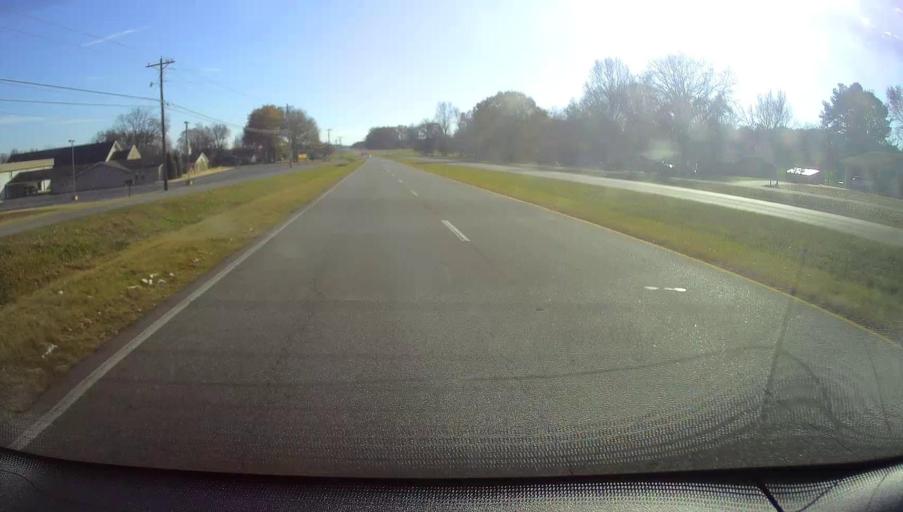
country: US
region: Alabama
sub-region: Limestone County
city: Athens
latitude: 34.7266
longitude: -86.9570
